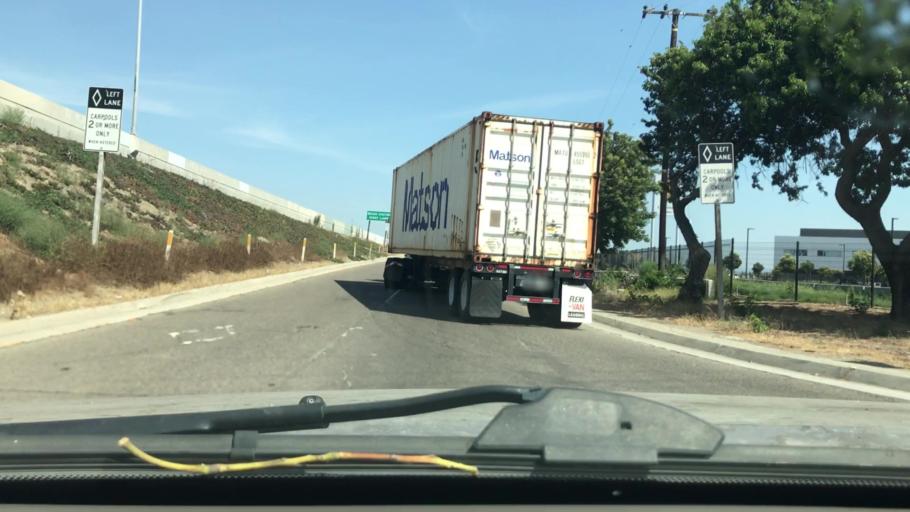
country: US
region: California
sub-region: Los Angeles County
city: Carson
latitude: 33.8526
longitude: -118.2802
